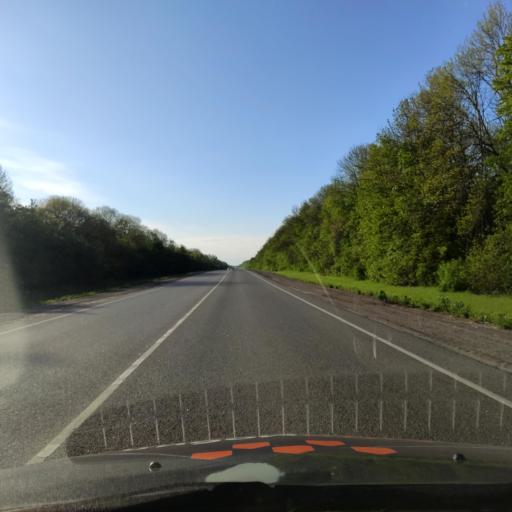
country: RU
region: Lipetsk
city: Yelets
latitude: 52.5756
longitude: 38.6483
